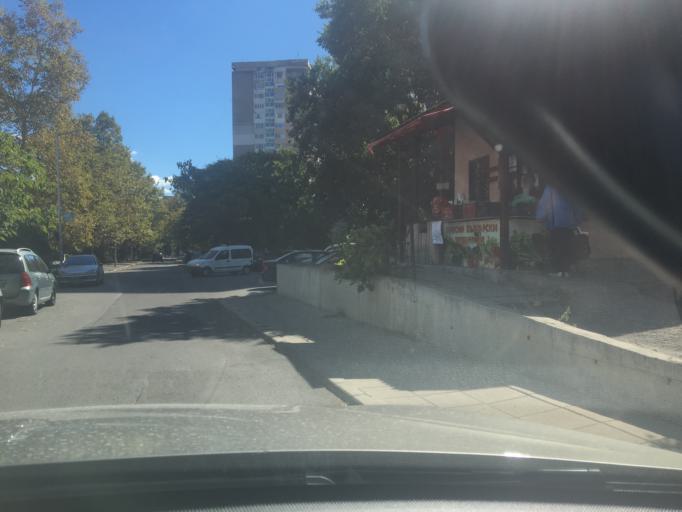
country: BG
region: Burgas
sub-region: Obshtina Burgas
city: Burgas
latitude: 42.5061
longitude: 27.4744
